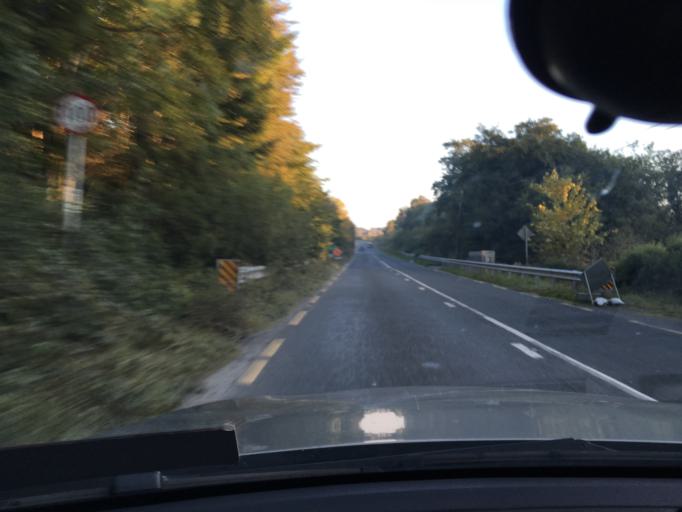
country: IE
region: Connaught
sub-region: County Galway
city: Moycullen
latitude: 53.3766
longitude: -9.2453
